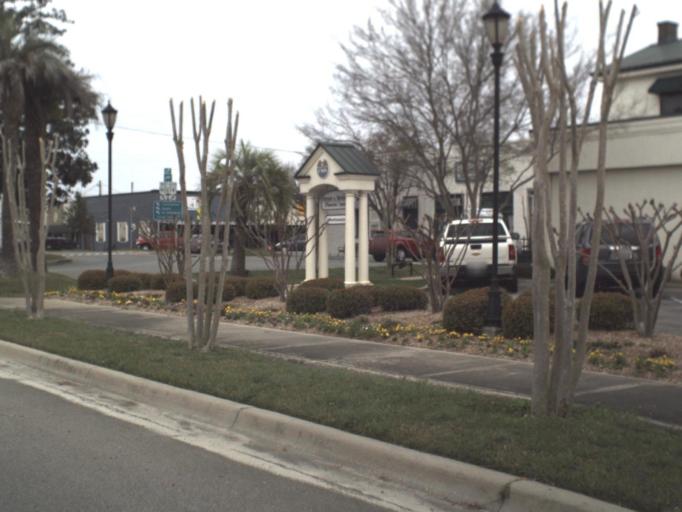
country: US
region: Florida
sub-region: Jefferson County
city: Monticello
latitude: 30.5451
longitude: -83.8694
